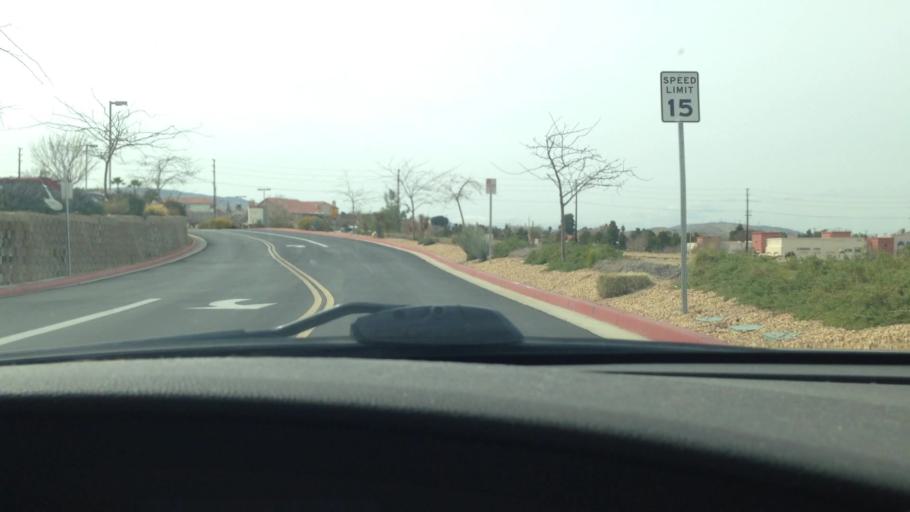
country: US
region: California
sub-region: Los Angeles County
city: Desert View Highlands
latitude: 34.5843
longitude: -118.1448
